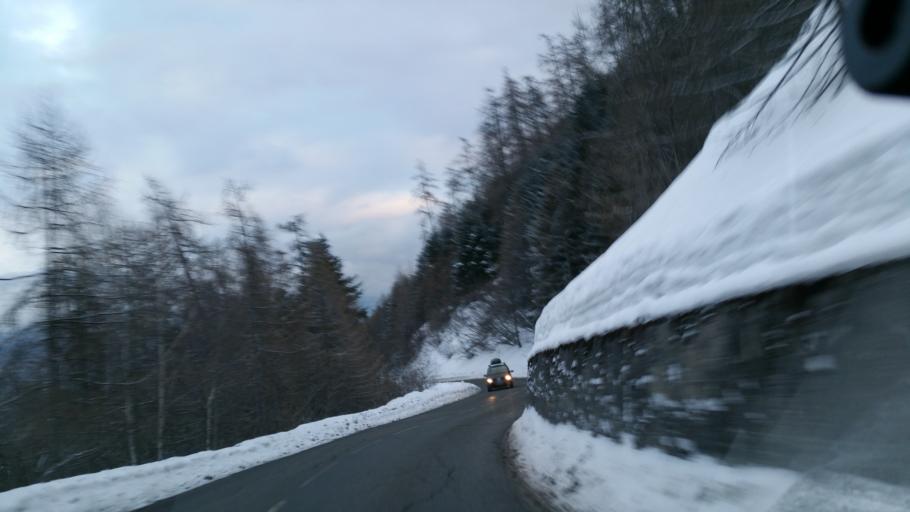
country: FR
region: Rhone-Alpes
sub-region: Departement de la Savoie
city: Villargondran
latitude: 45.2349
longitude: 6.4039
